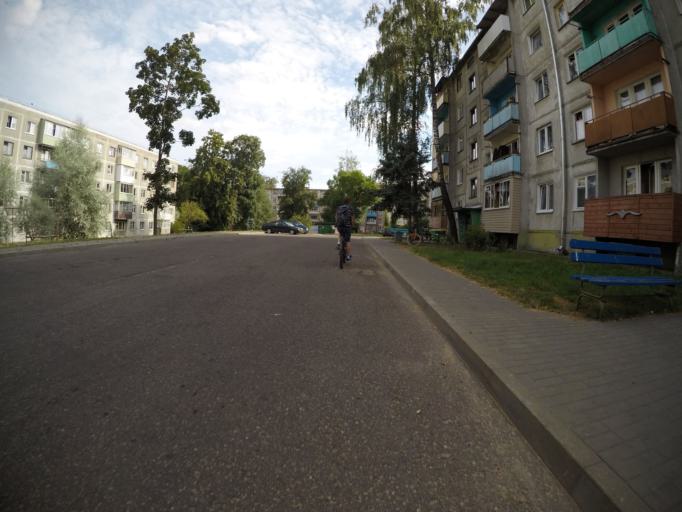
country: BY
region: Grodnenskaya
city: Hrodna
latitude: 53.6965
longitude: 23.8290
